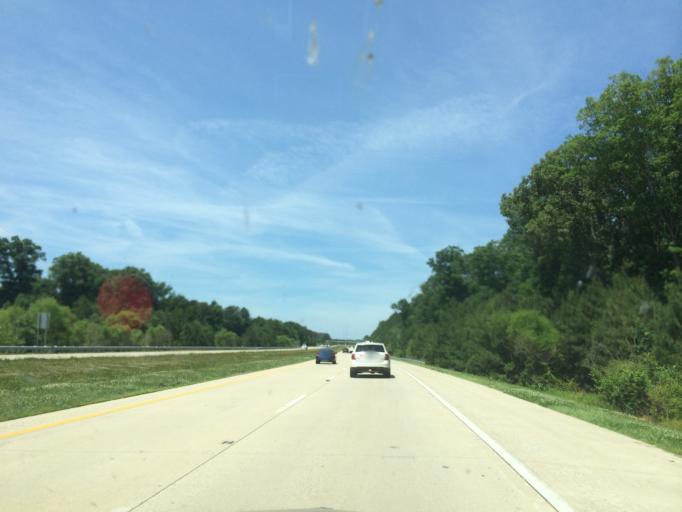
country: US
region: Maryland
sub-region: Wicomico County
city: Salisbury
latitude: 38.4043
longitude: -75.6083
